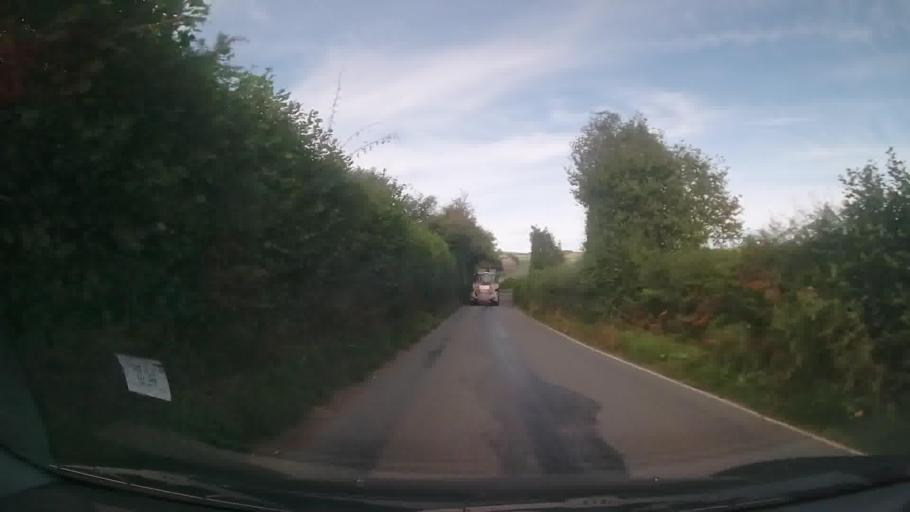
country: GB
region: Wales
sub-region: Sir Powys
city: Whitton
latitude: 52.2922
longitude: -3.0746
